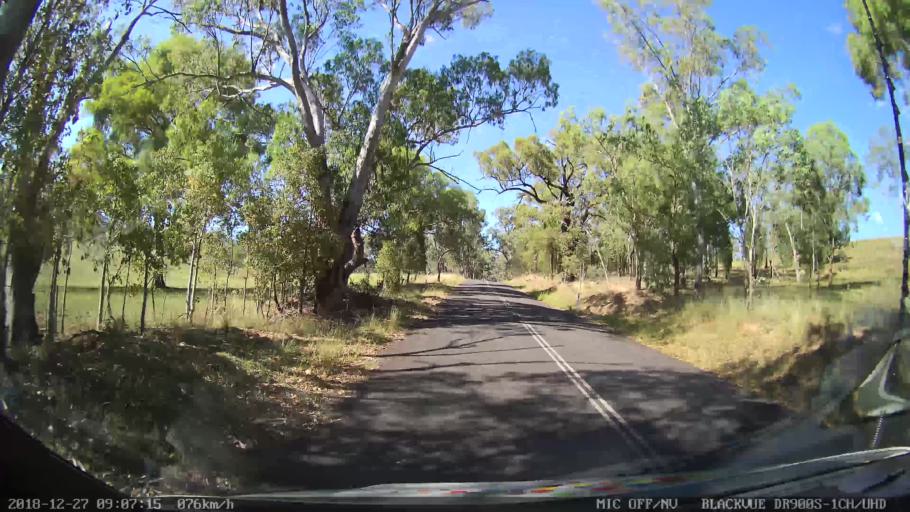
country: AU
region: New South Wales
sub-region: Lithgow
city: Portland
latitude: -33.1269
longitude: 150.1582
